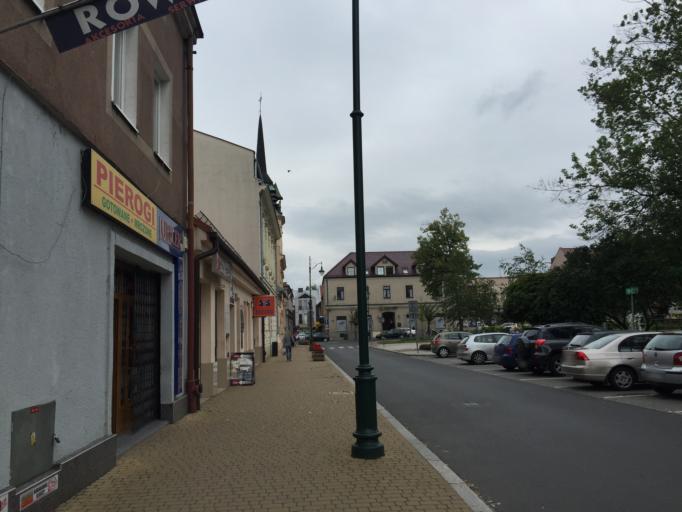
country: PL
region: Lesser Poland Voivodeship
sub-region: Powiat krakowski
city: Skawina
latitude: 49.9749
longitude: 19.8253
